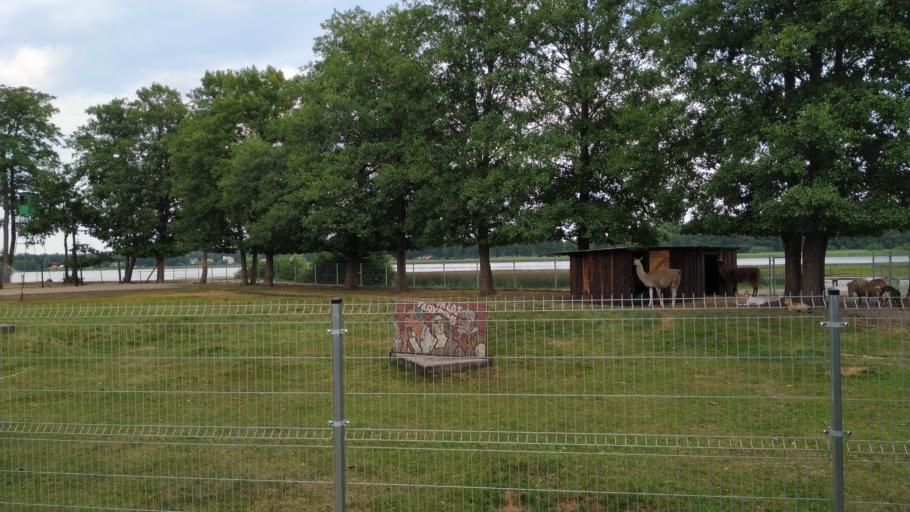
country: LT
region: Alytaus apskritis
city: Druskininkai
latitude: 54.0241
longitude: 24.0795
